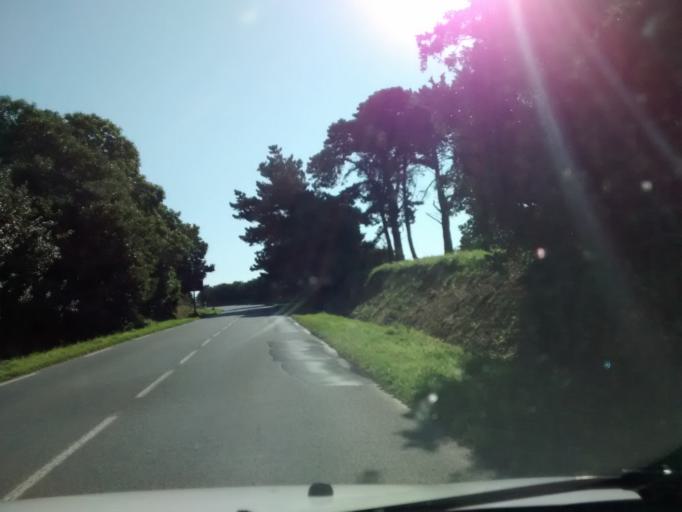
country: FR
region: Brittany
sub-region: Departement des Cotes-d'Armor
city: Pleumeur-Gautier
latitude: 48.8272
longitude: -3.1766
